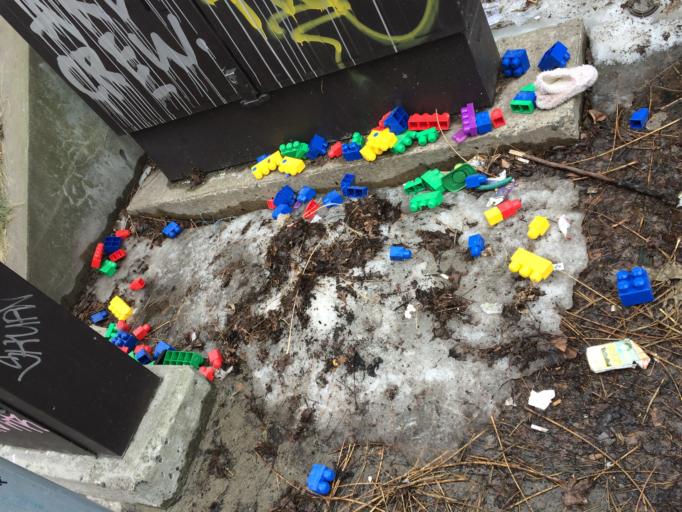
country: CA
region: Quebec
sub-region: Montreal
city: Montreal
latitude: 45.5088
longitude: -73.5594
